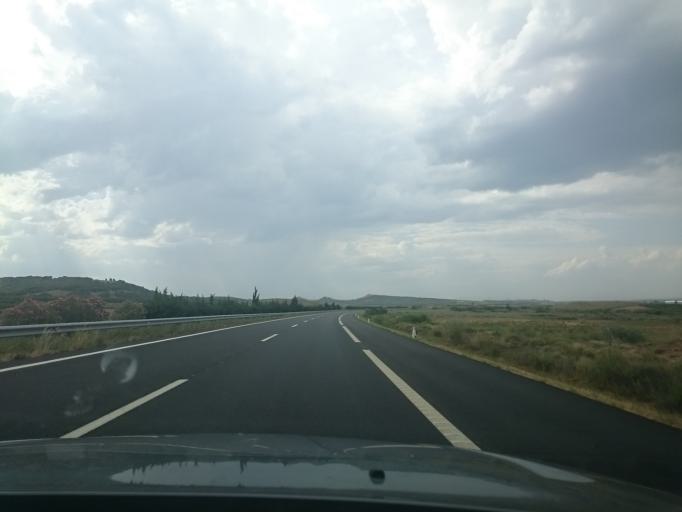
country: ES
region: La Rioja
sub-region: Provincia de La Rioja
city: Aldeanueva de Ebro
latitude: 42.2524
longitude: -1.9152
